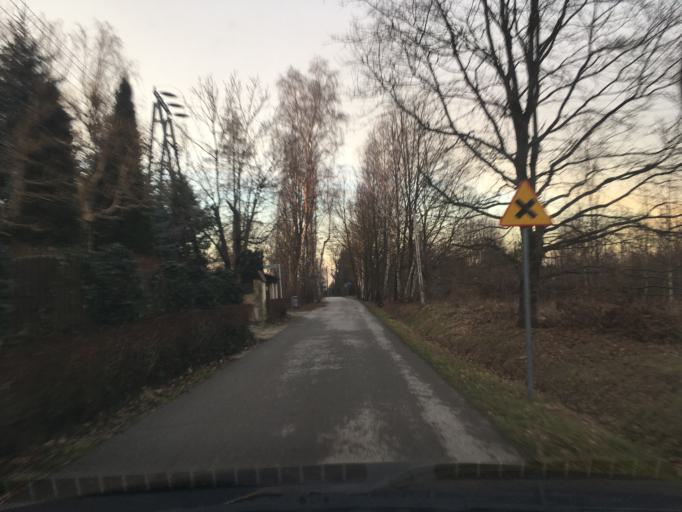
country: PL
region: Masovian Voivodeship
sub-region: Powiat piaseczynski
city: Lesznowola
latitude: 52.0396
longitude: 20.9610
